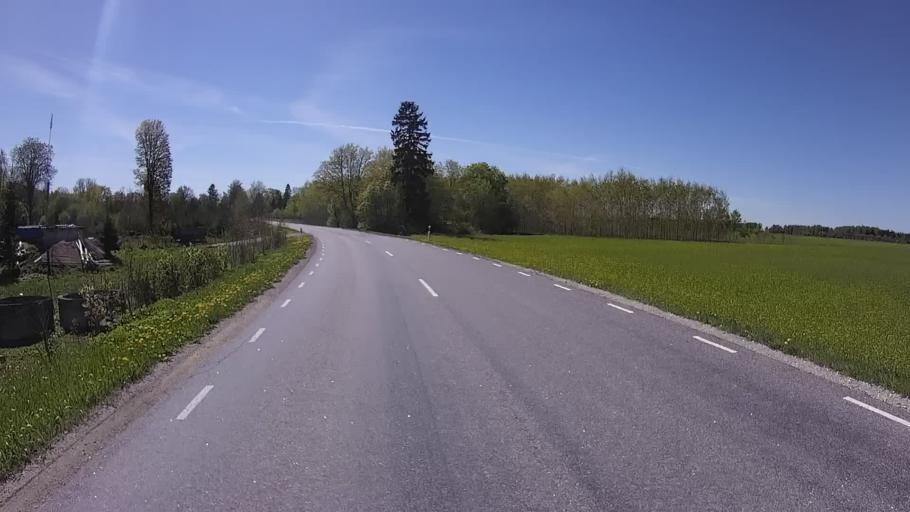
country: EE
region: Harju
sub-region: Rae vald
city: Vaida
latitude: 59.0721
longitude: 25.1602
